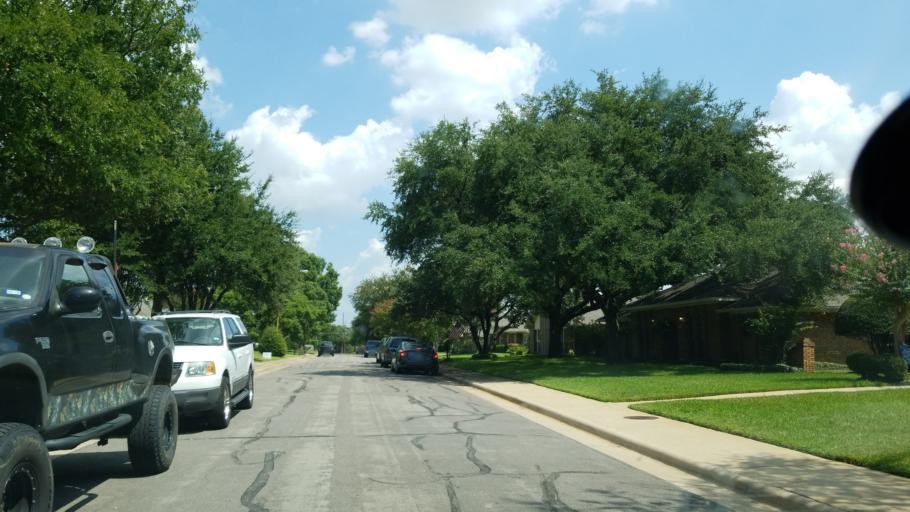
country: US
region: Texas
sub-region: Dallas County
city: Richardson
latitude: 32.9181
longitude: -96.7206
